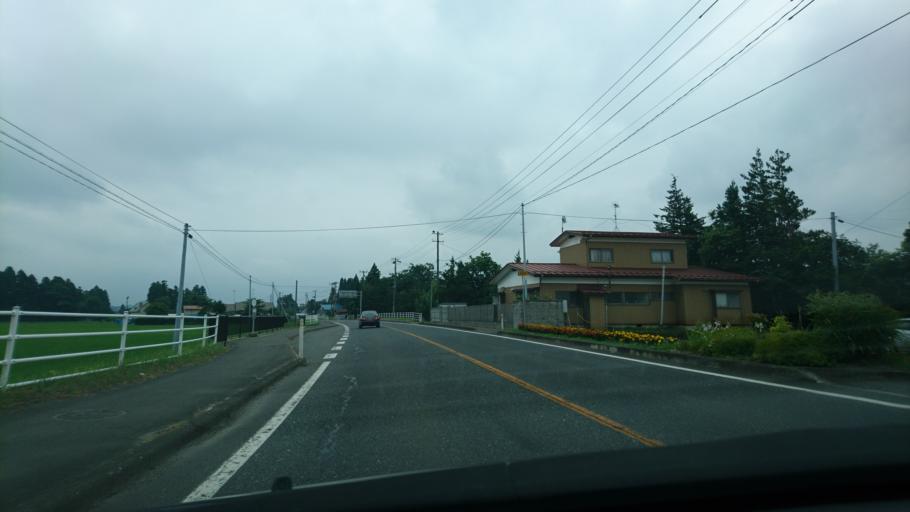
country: JP
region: Miyagi
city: Furukawa
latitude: 38.7014
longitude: 140.8395
